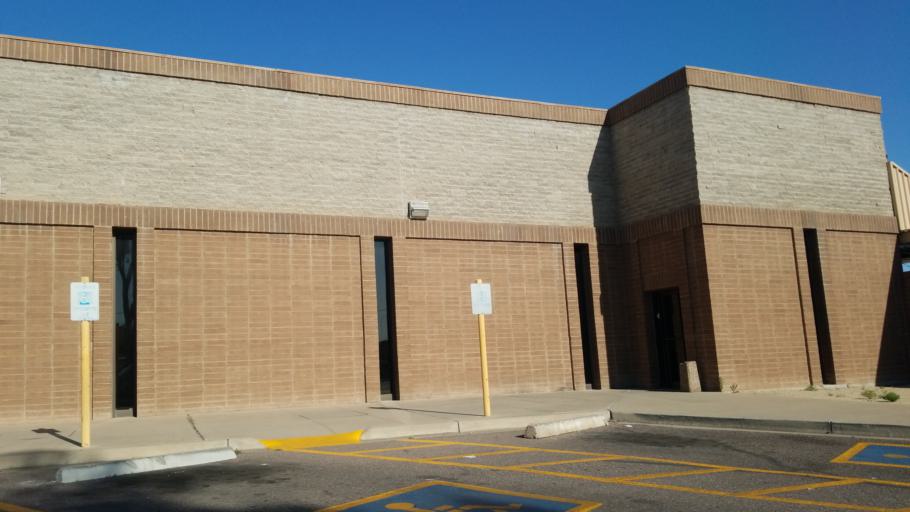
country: US
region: Arizona
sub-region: Maricopa County
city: Glendale
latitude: 33.5325
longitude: -112.1771
